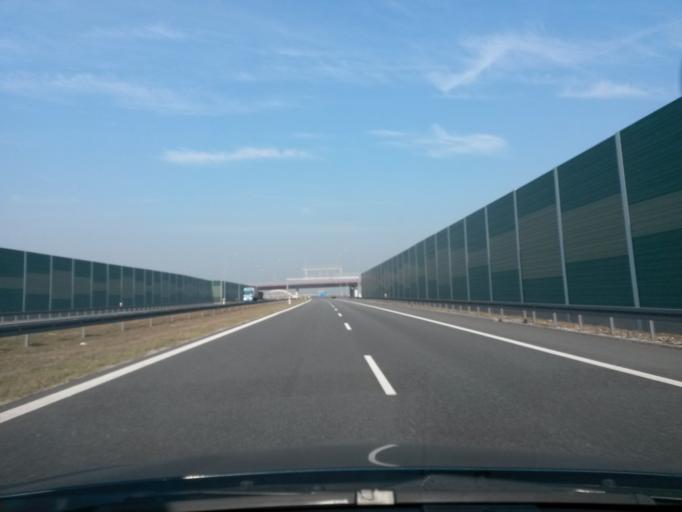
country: PL
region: Lodz Voivodeship
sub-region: Powiat kutnowski
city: Krzyzanow
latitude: 52.2167
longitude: 19.4751
